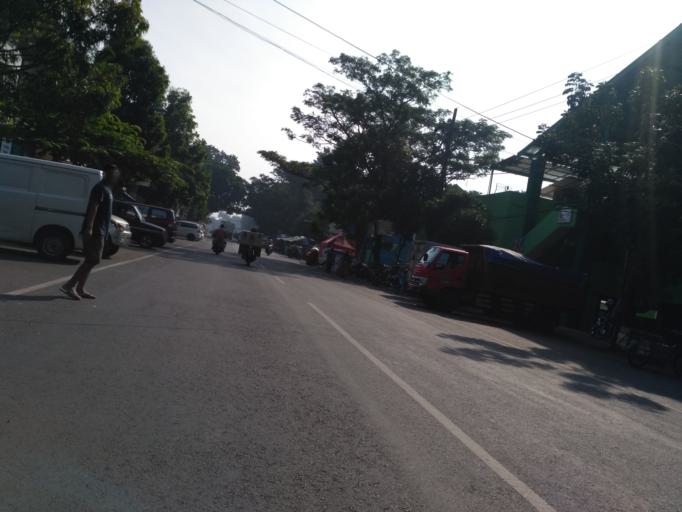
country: ID
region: East Java
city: Malang
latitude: -7.9773
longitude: 112.6202
